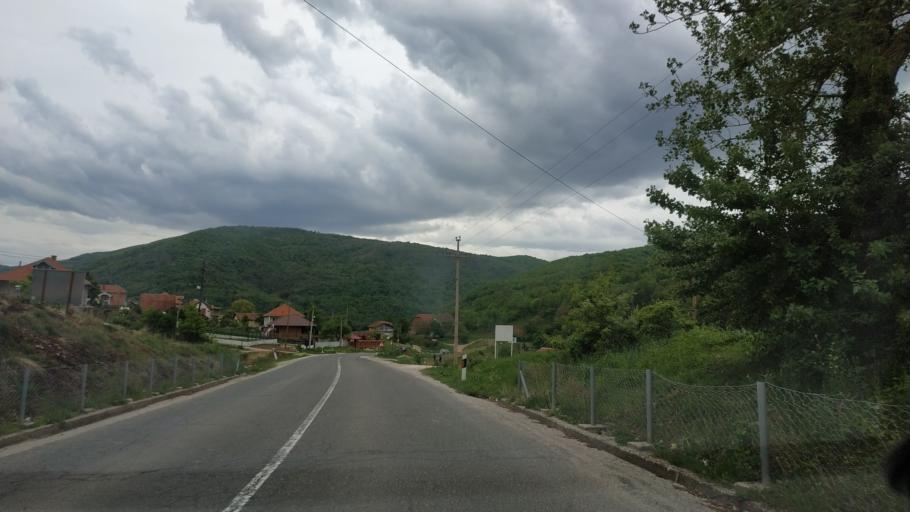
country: RS
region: Central Serbia
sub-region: Nisavski Okrug
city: Aleksinac
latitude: 43.6413
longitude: 21.7135
